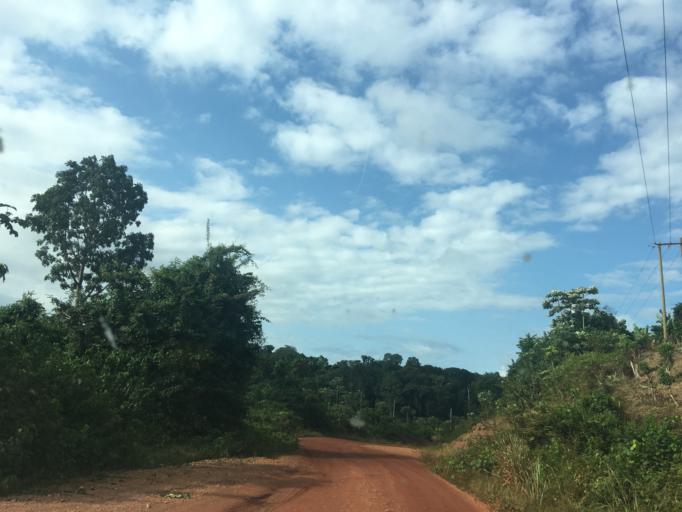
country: GH
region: Western
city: Wassa-Akropong
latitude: 5.9600
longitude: -2.4286
